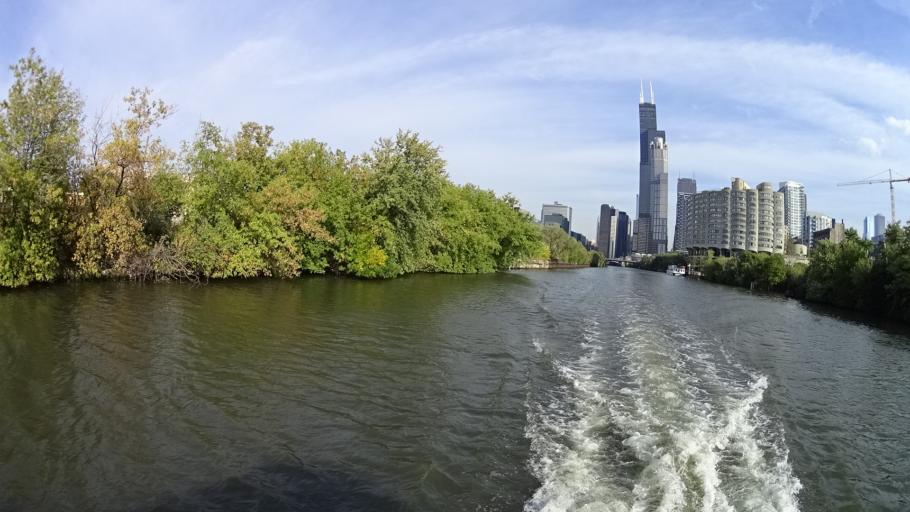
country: US
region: Illinois
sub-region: Cook County
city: Chicago
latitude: 41.8689
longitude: -87.6350
